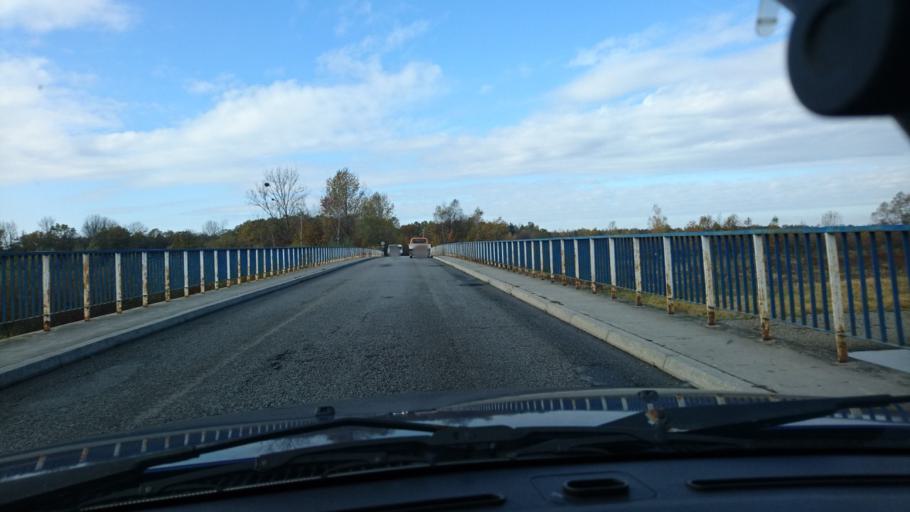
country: PL
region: Lesser Poland Voivodeship
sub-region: Powiat oswiecimski
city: Nowa Wies
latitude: 49.9383
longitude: 19.1975
